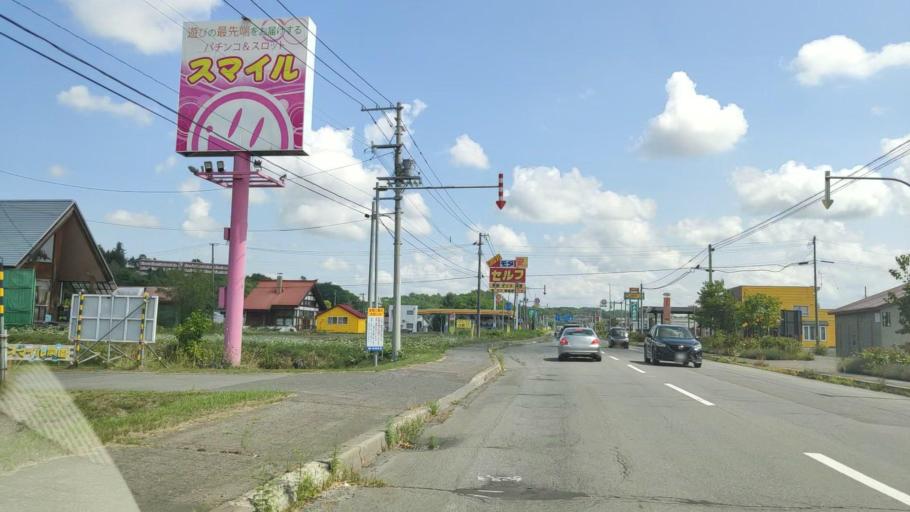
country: JP
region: Hokkaido
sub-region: Asahikawa-shi
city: Asahikawa
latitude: 43.5953
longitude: 142.4604
